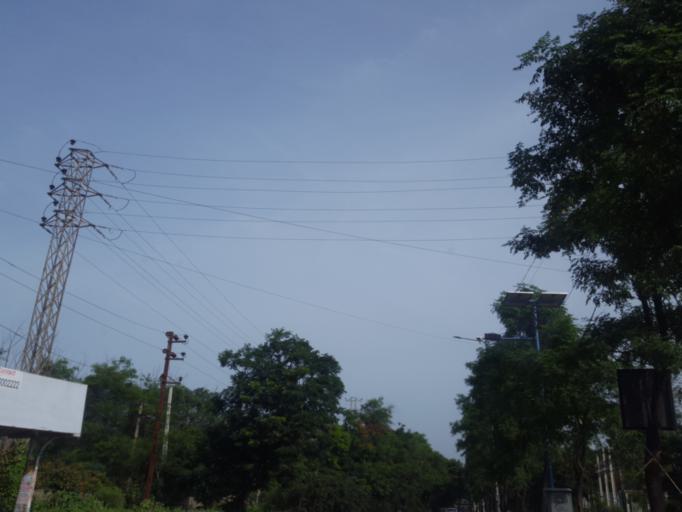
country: IN
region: Telangana
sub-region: Medak
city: Serilingampalle
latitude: 17.4569
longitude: 78.3397
